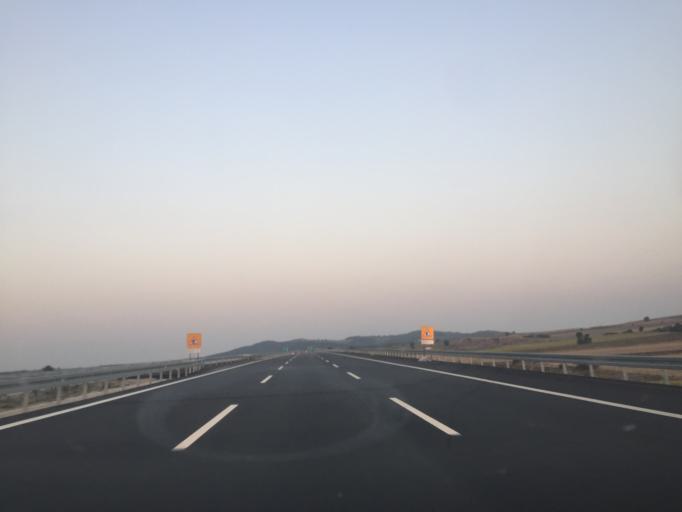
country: TR
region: Bursa
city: Mahmudiye
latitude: 40.2588
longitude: 28.6859
